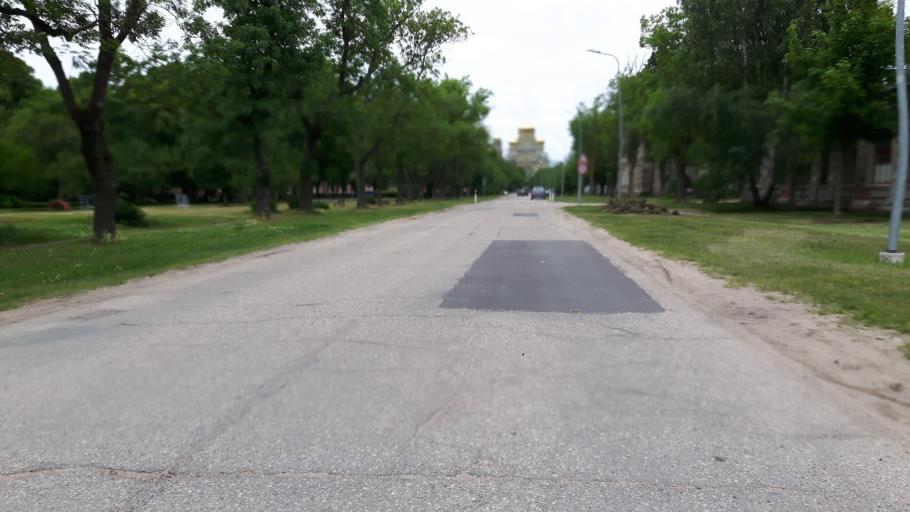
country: LV
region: Liepaja
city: Vec-Liepaja
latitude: 56.5486
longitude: 21.0115
